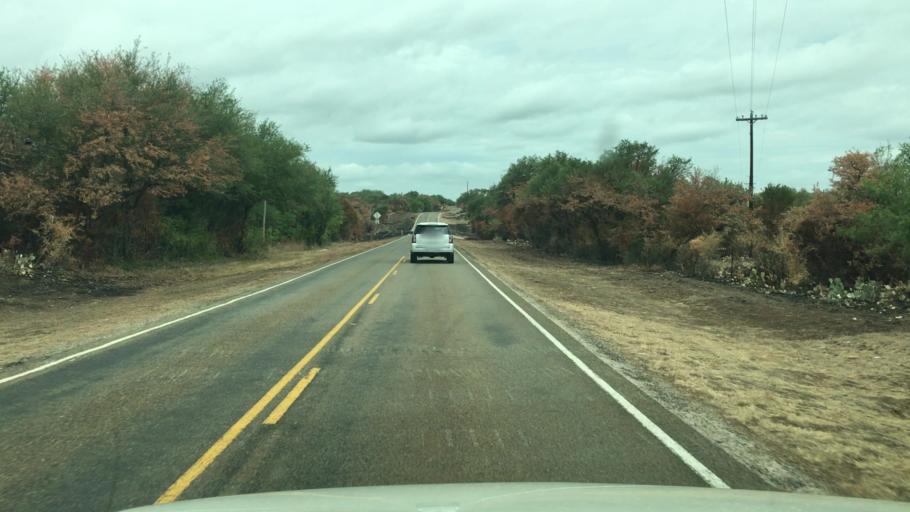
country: US
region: Texas
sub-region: Llano County
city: Horseshoe Bay
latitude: 30.4792
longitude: -98.4199
